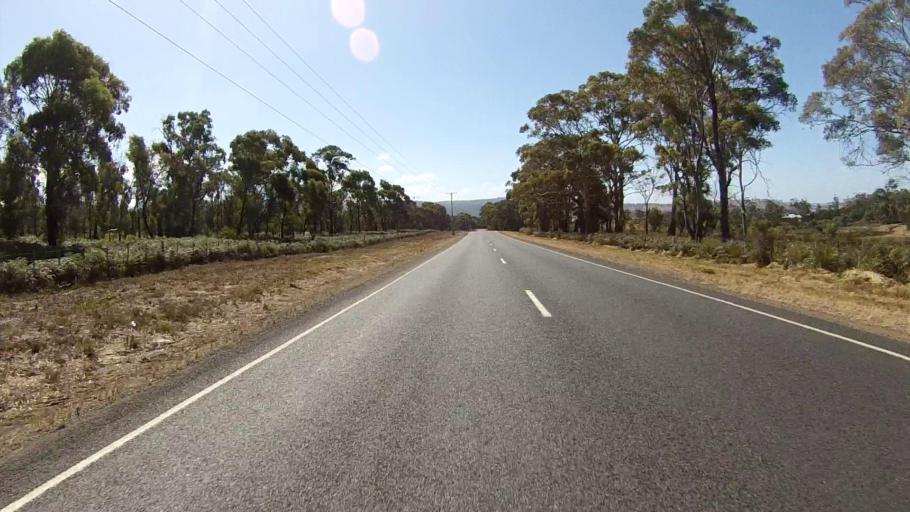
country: AU
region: Tasmania
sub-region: Sorell
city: Sorell
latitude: -42.5341
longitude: 147.8974
